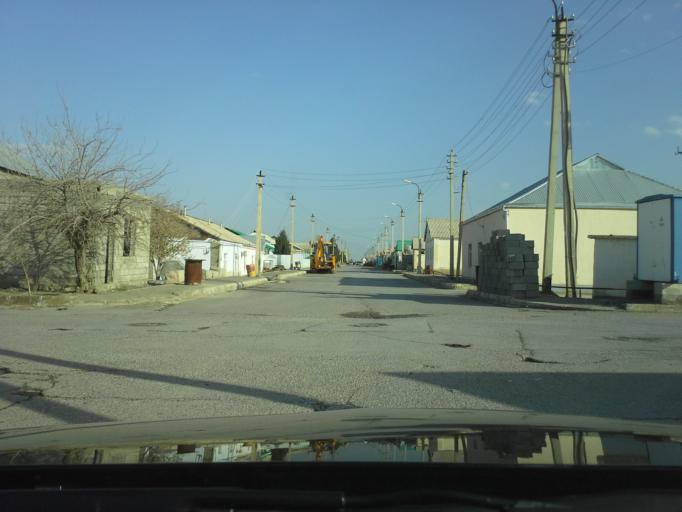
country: TM
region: Ahal
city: Abadan
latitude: 38.0185
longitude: 58.2302
